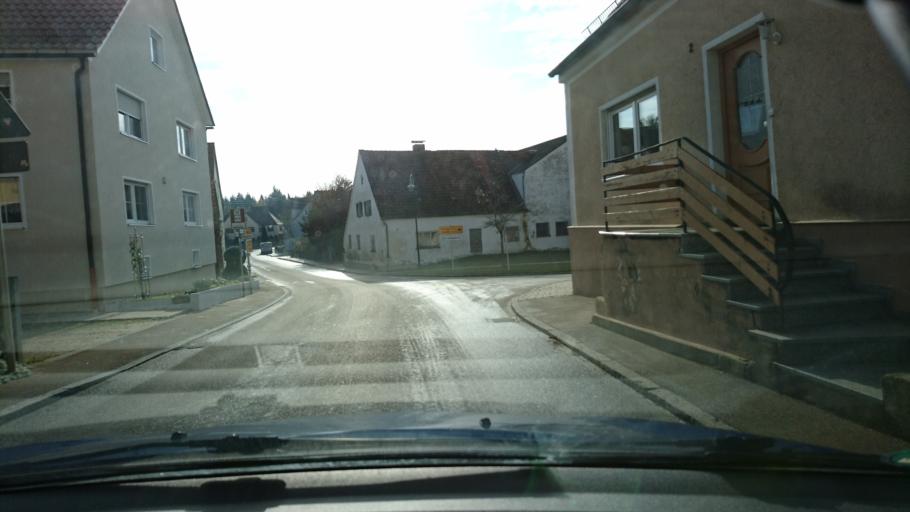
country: DE
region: Bavaria
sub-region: Swabia
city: Amerdingen
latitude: 48.7258
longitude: 10.4863
